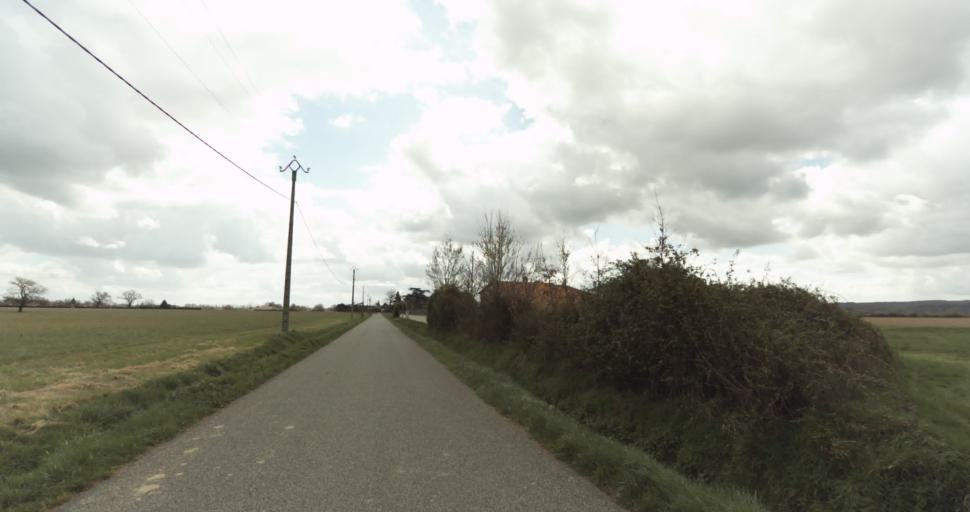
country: FR
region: Midi-Pyrenees
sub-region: Departement de la Haute-Garonne
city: Auterive
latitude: 43.3386
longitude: 1.4717
